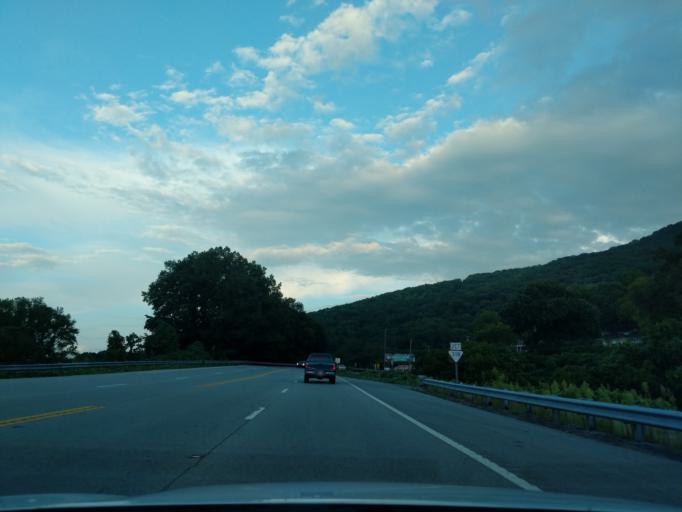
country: US
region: Tennessee
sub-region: Hamilton County
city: Lookout Mountain
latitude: 35.0212
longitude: -85.3556
